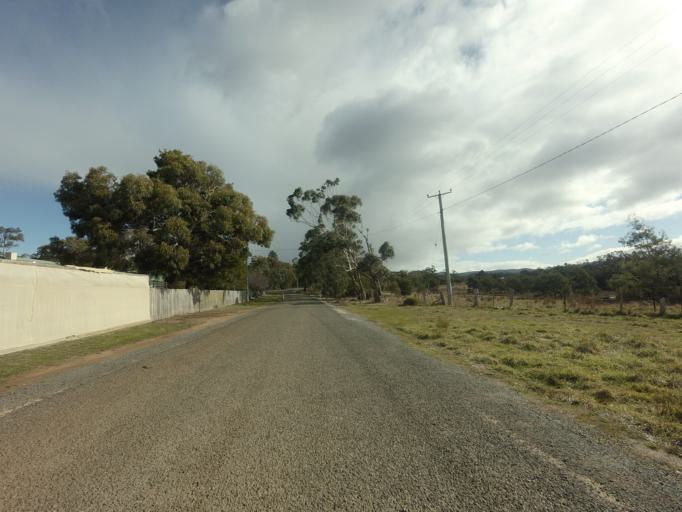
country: AU
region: Tasmania
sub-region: Sorell
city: Sorell
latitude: -42.3253
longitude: 147.9635
